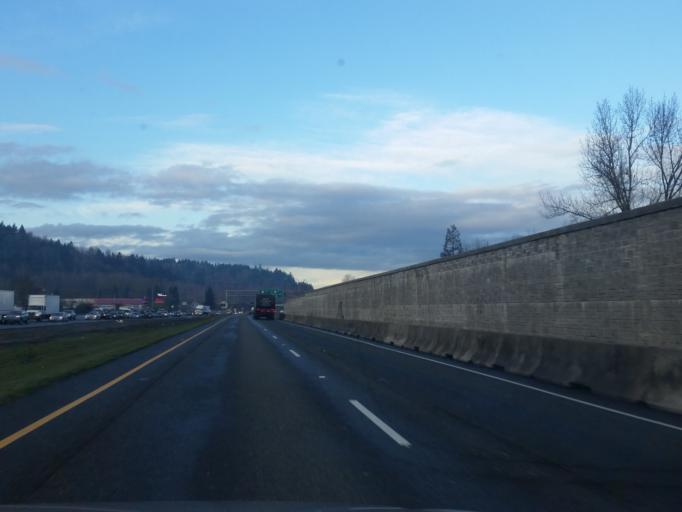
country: US
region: Washington
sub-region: King County
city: Algona
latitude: 47.2898
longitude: -122.2580
